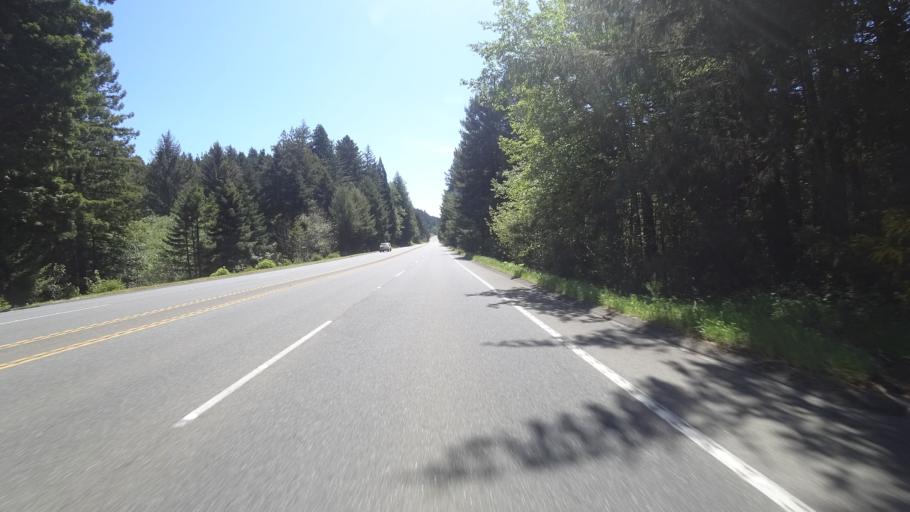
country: US
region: California
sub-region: Humboldt County
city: Westhaven-Moonstone
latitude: 41.0502
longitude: -124.1220
